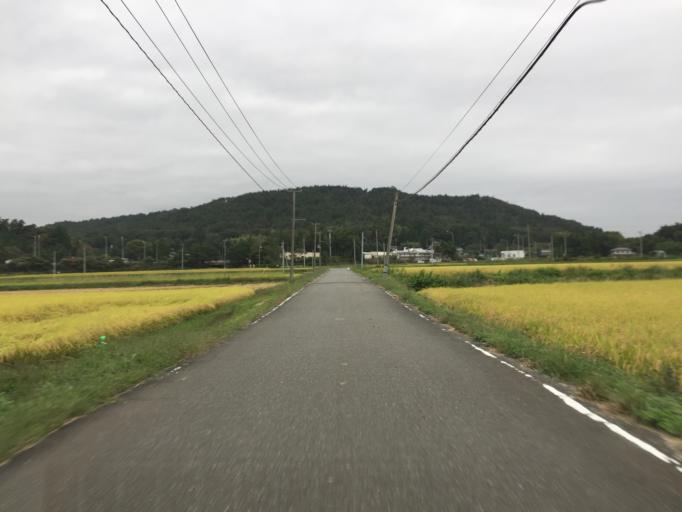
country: JP
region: Fukushima
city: Nihommatsu
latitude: 37.6587
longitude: 140.4447
